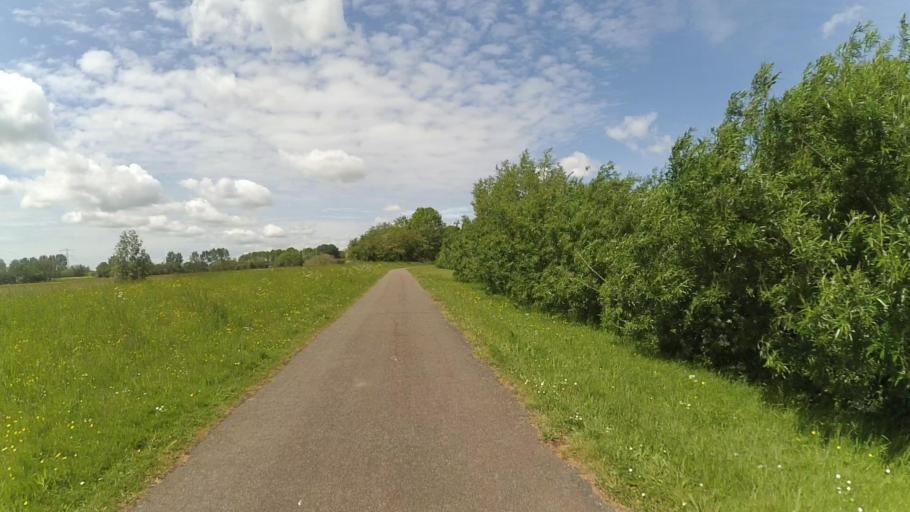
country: NL
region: South Holland
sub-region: Gemeente Spijkenisse
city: Spijkenisse
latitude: 51.8448
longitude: 4.2559
